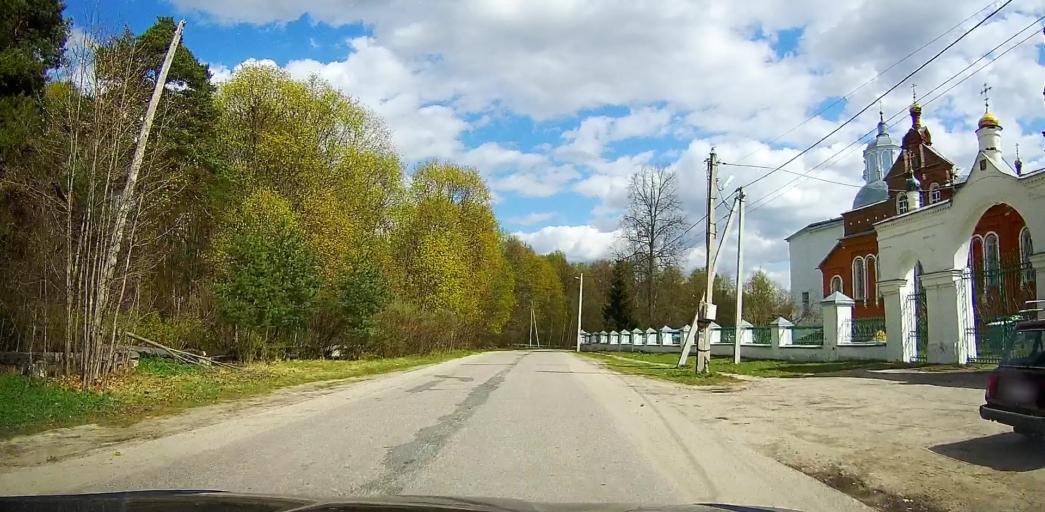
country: RU
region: Moskovskaya
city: Davydovo
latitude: 55.6480
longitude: 38.7562
